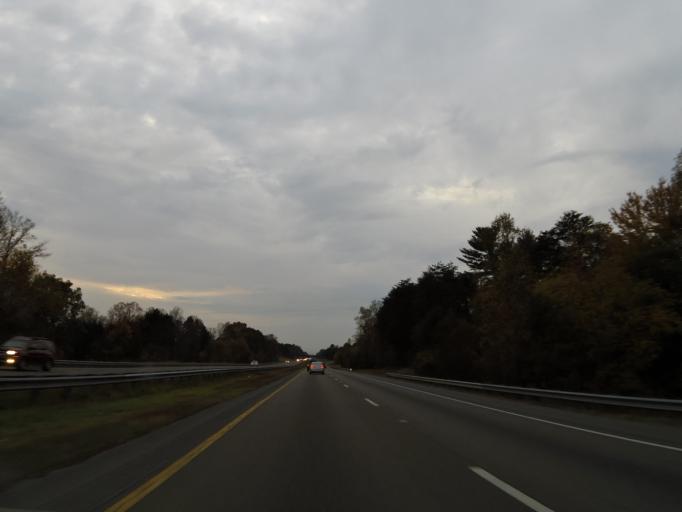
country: US
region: North Carolina
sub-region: Burke County
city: Hildebran
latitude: 35.7073
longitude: -81.4324
